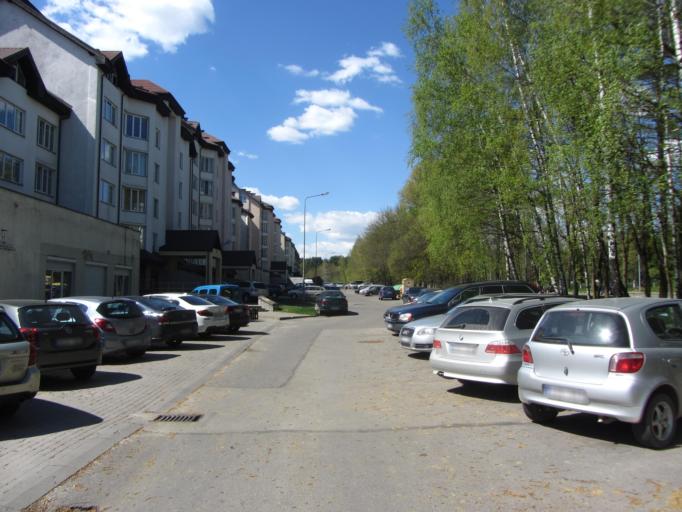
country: LT
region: Vilnius County
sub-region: Vilnius
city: Fabijoniskes
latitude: 54.7505
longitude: 25.2759
